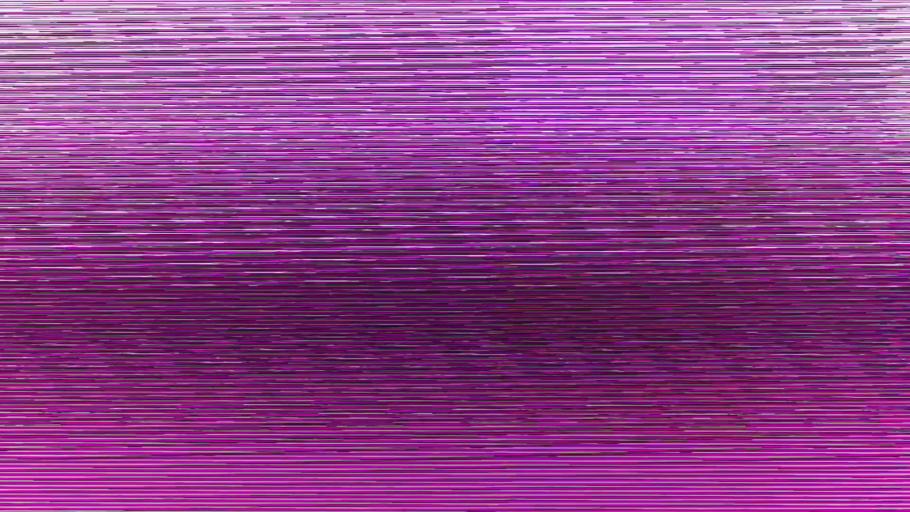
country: US
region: Michigan
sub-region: Washtenaw County
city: Ypsilanti
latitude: 42.2339
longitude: -83.6141
